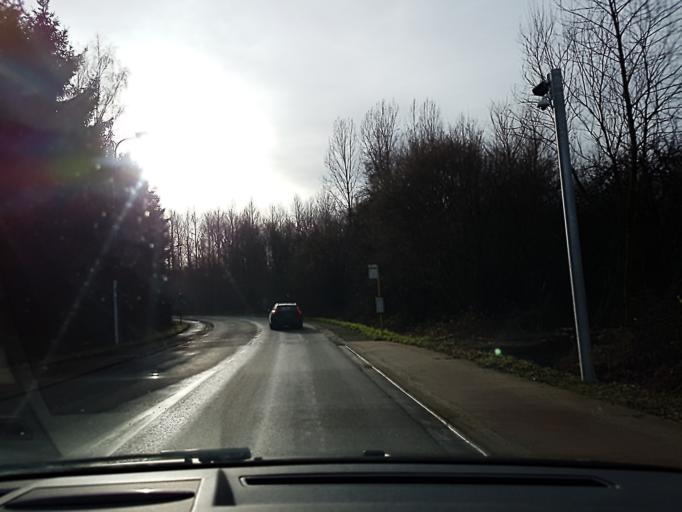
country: BE
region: Flanders
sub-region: Provincie Vlaams-Brabant
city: Haacht
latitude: 50.9723
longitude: 4.6604
